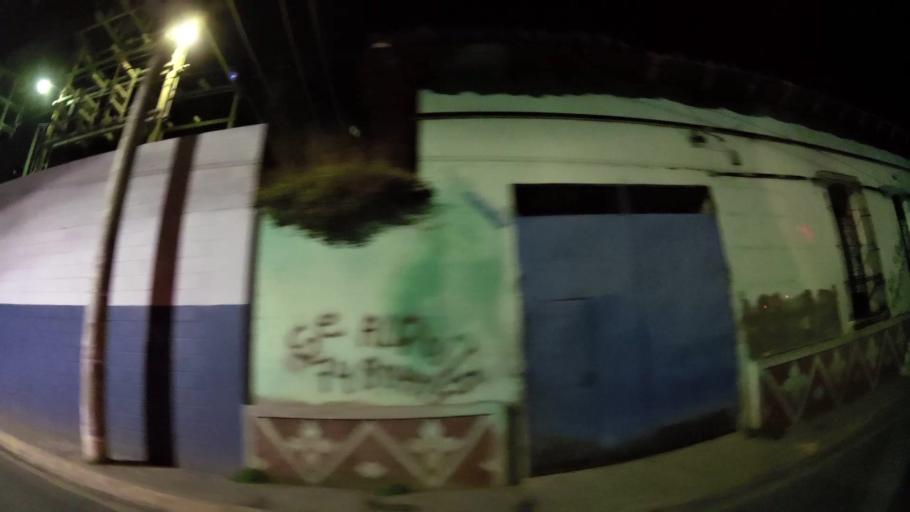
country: SV
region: La Paz
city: Zacatecoluca
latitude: 13.5079
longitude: -88.8686
